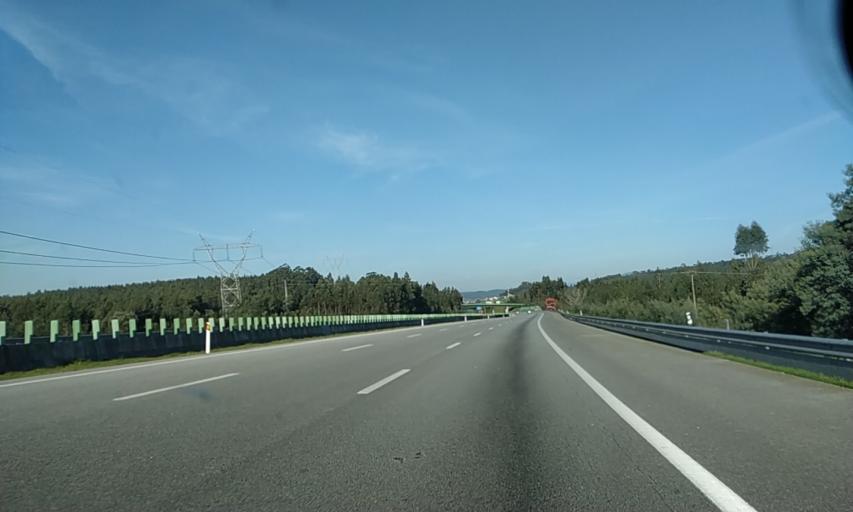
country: PT
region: Coimbra
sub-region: Condeixa-A-Nova
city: Condeixa-a-Nova
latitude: 40.1769
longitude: -8.4941
